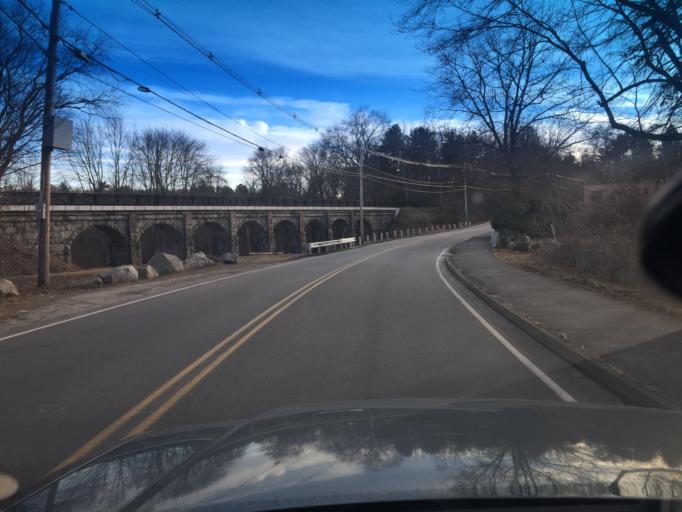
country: US
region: Massachusetts
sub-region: Middlesex County
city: Holliston
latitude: 42.2098
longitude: -71.4178
